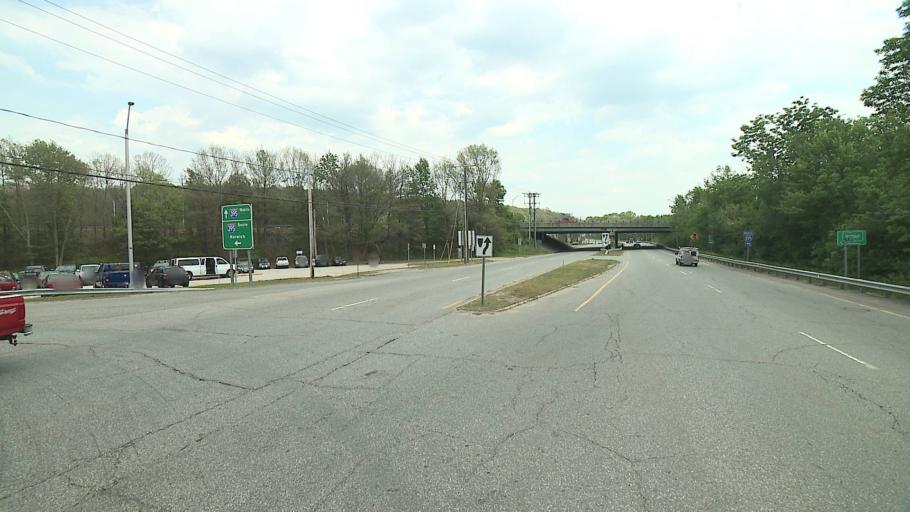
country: US
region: Connecticut
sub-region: Windham County
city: Moosup
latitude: 41.7188
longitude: -71.8958
